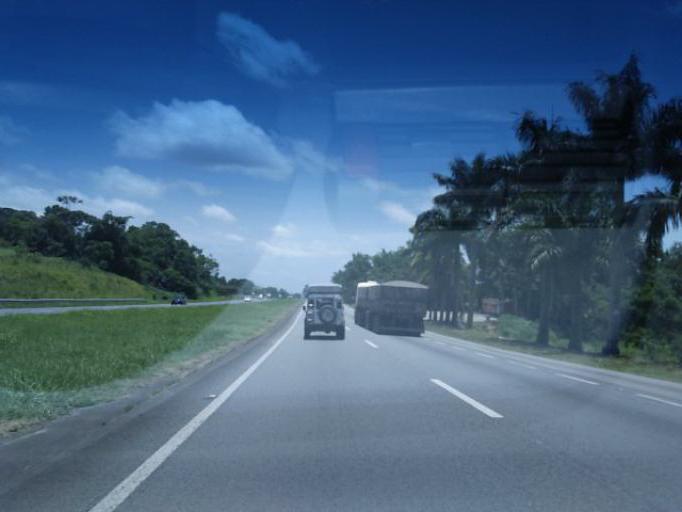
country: BR
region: Sao Paulo
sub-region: Juquia
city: Juquia
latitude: -24.3545
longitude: -47.6747
